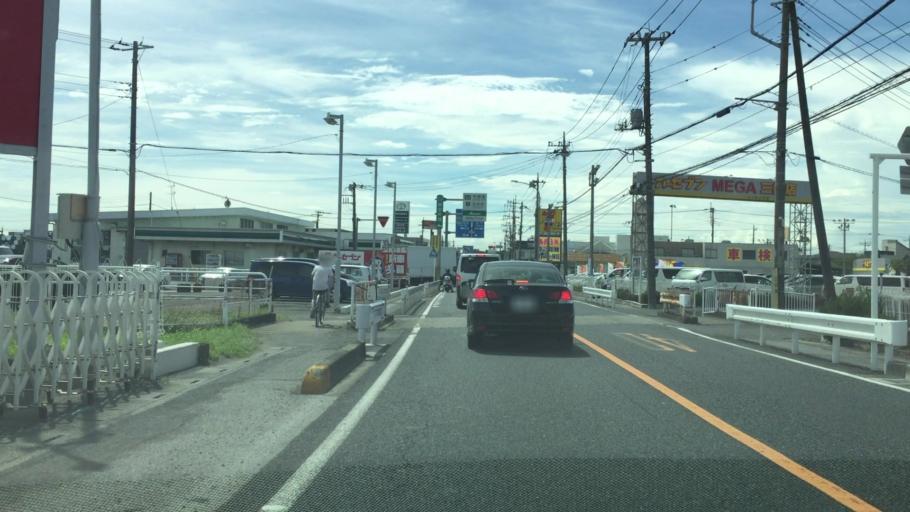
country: JP
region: Saitama
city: Yashio-shi
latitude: 35.8498
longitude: 139.8559
